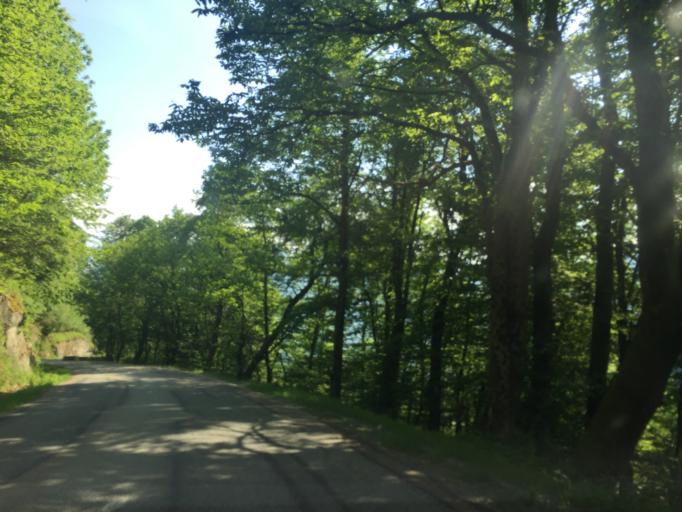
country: FR
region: Rhone-Alpes
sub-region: Departement de la Savoie
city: Aiton
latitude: 45.5225
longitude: 6.3263
